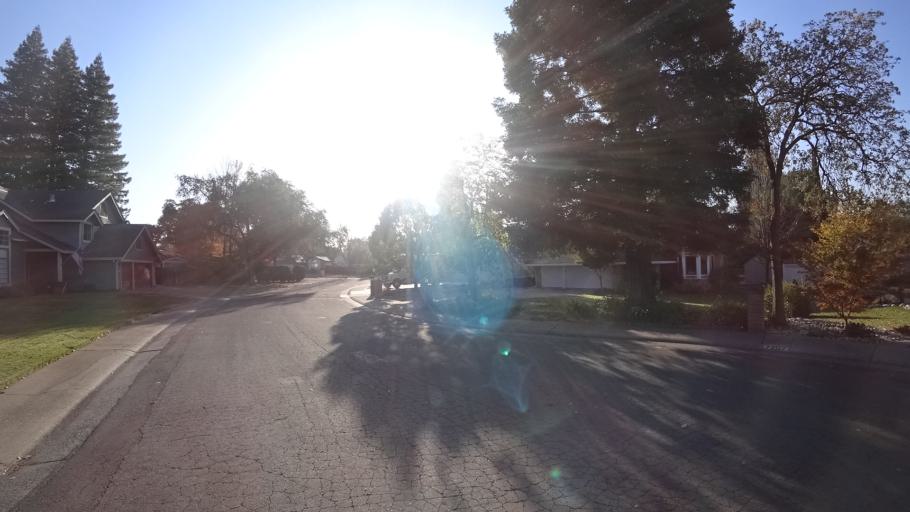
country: US
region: California
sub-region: Sacramento County
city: Citrus Heights
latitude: 38.6972
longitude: -121.2608
